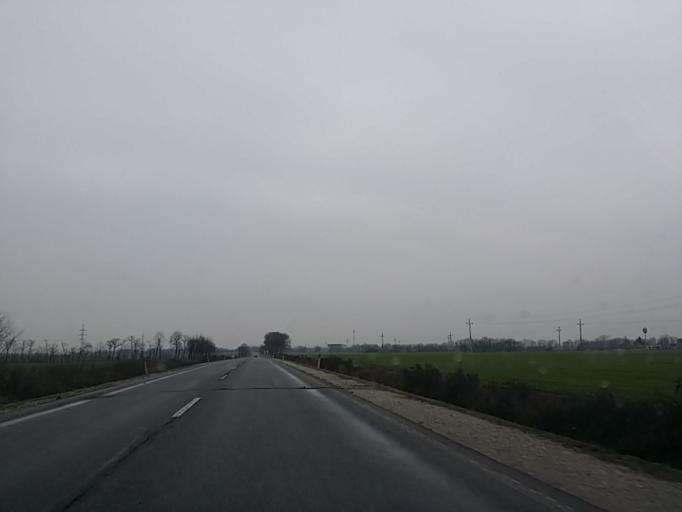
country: HU
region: Borsod-Abauj-Zemplen
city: Mezokovesd
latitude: 47.8235
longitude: 20.5830
